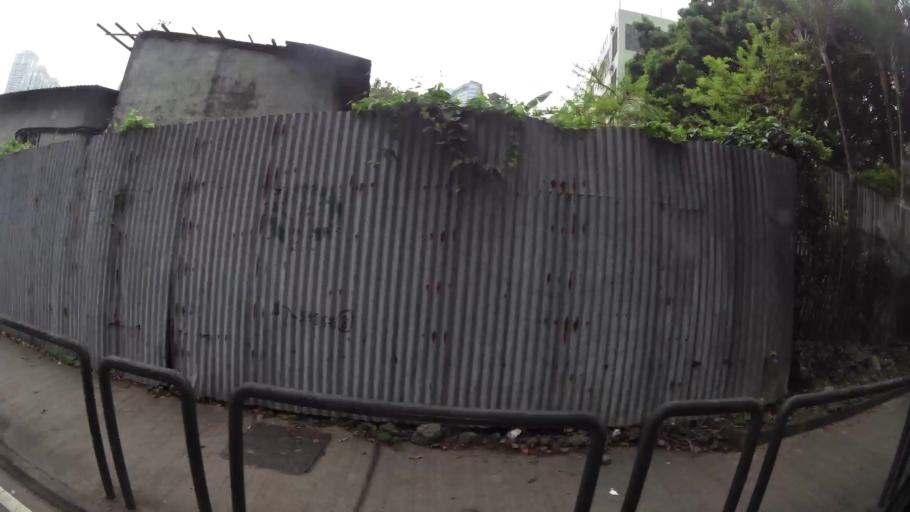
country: MO
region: Macau
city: Macau
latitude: 22.1622
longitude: 113.5594
